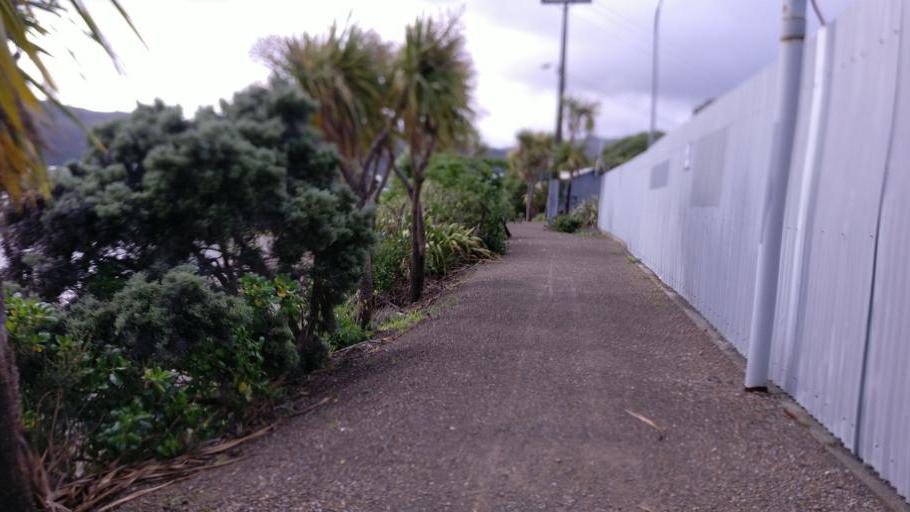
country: NZ
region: Wellington
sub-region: Lower Hutt City
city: Lower Hutt
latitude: -41.2341
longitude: 174.8977
